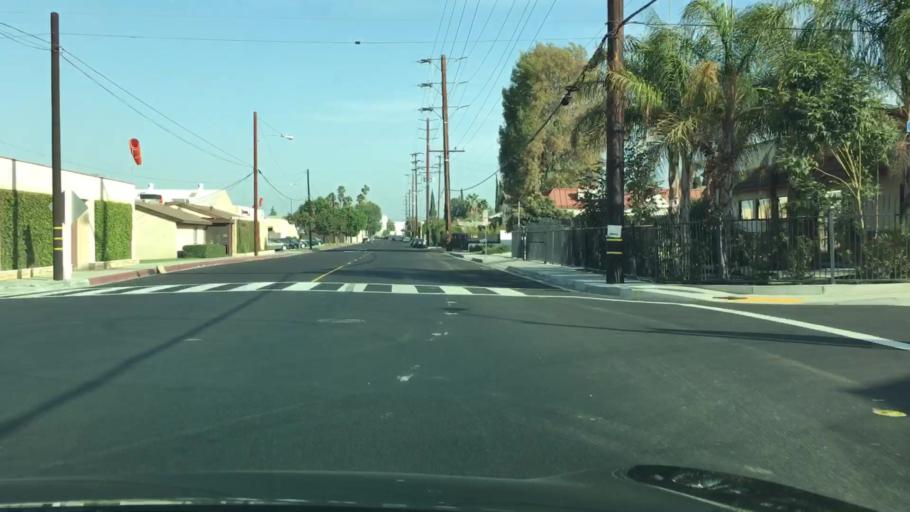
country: US
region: California
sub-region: Los Angeles County
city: Avocado Heights
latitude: 34.0201
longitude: -117.9780
